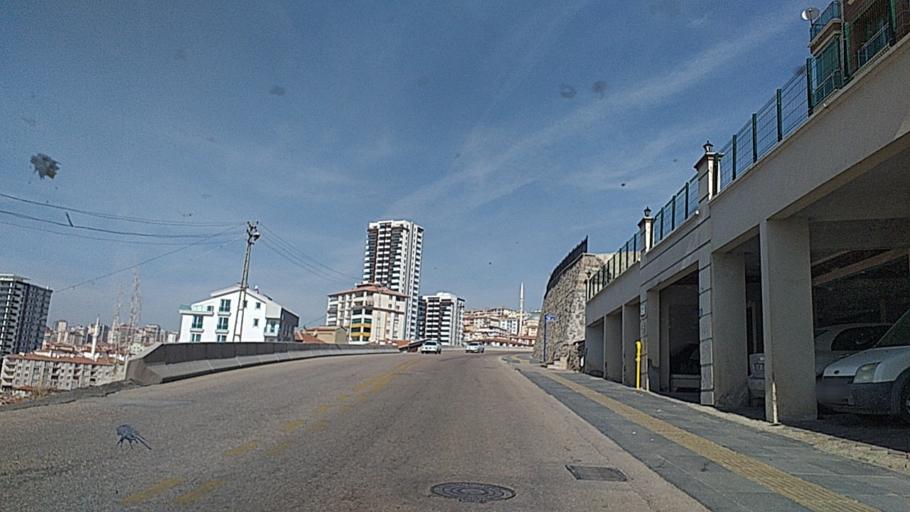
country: TR
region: Ankara
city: Ankara
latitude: 39.9893
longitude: 32.8123
